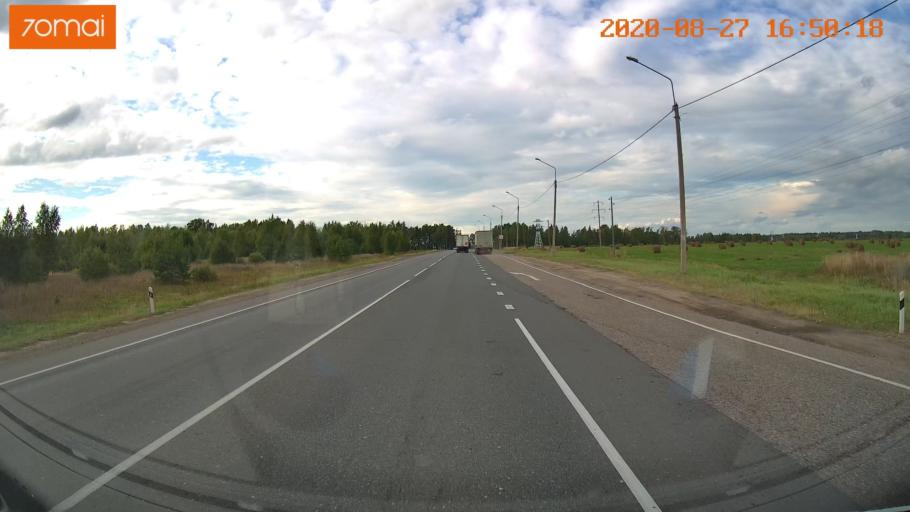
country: RU
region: Vladimir
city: Suzdal'
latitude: 56.4531
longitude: 40.4607
